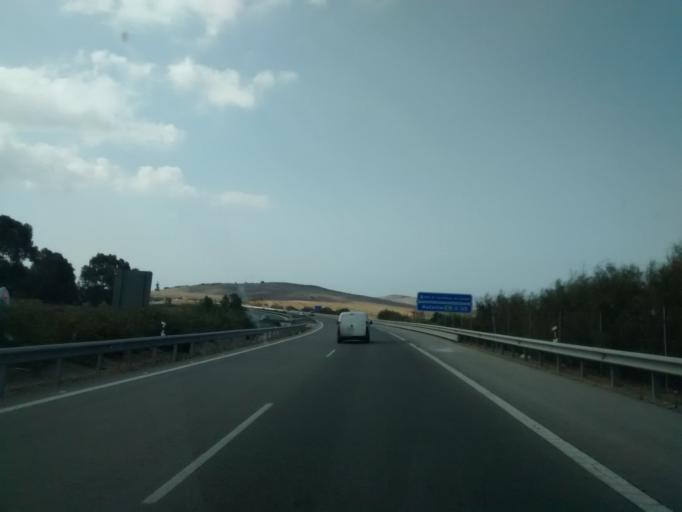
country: ES
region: Andalusia
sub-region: Provincia de Cadiz
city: Conil de la Frontera
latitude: 36.2660
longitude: -6.0292
